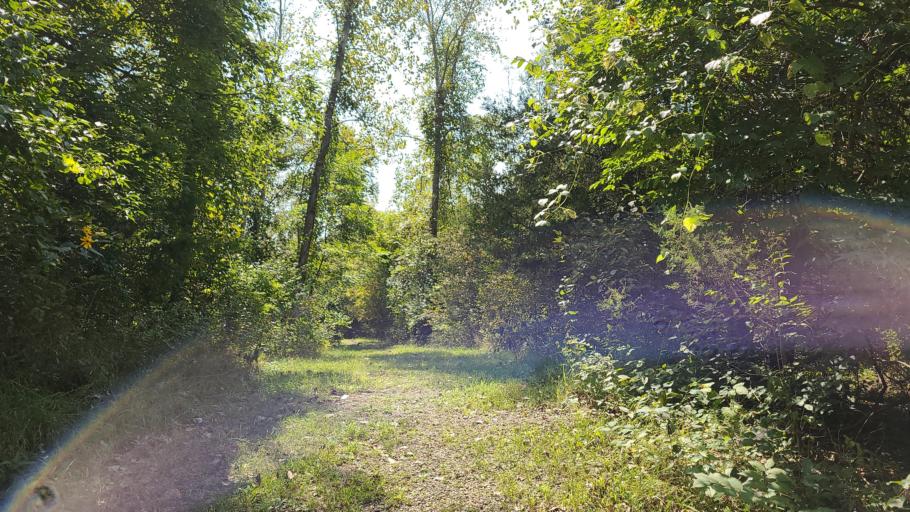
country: US
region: Kansas
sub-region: Douglas County
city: Lawrence
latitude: 38.9584
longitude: -95.3179
